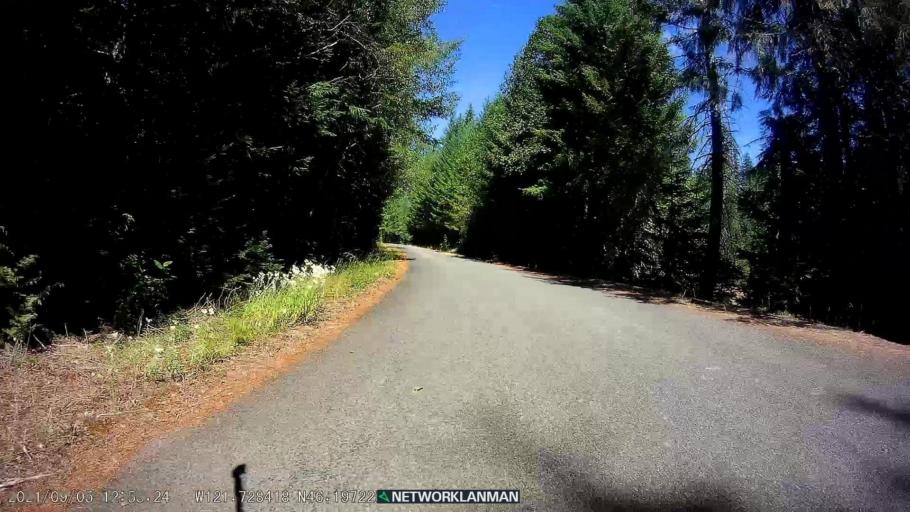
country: US
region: Washington
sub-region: Skamania County
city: Carson
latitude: 46.1971
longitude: -121.7284
